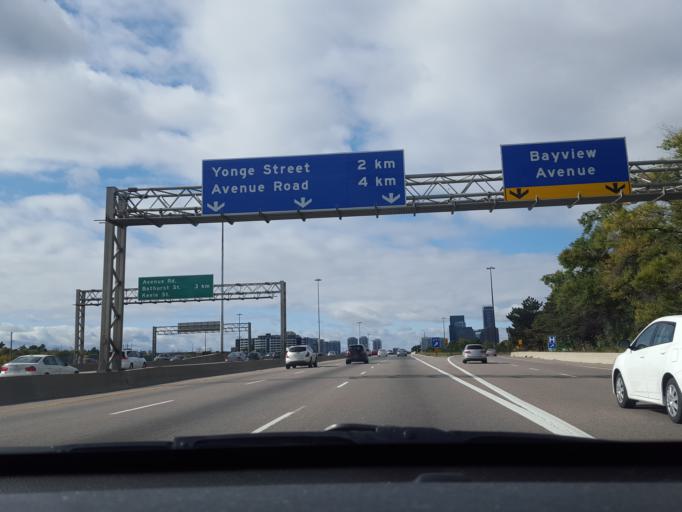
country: CA
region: Ontario
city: Willowdale
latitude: 43.7647
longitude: -79.3821
